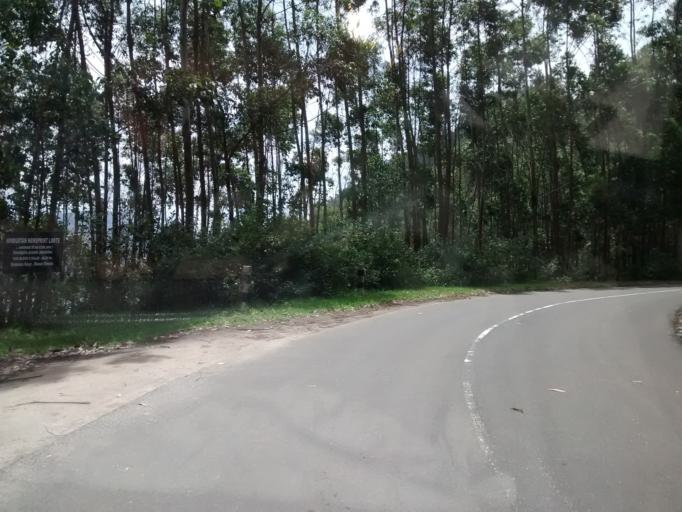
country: IN
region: Kerala
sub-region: Idukki
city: Munnar
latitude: 10.1243
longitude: 77.1570
